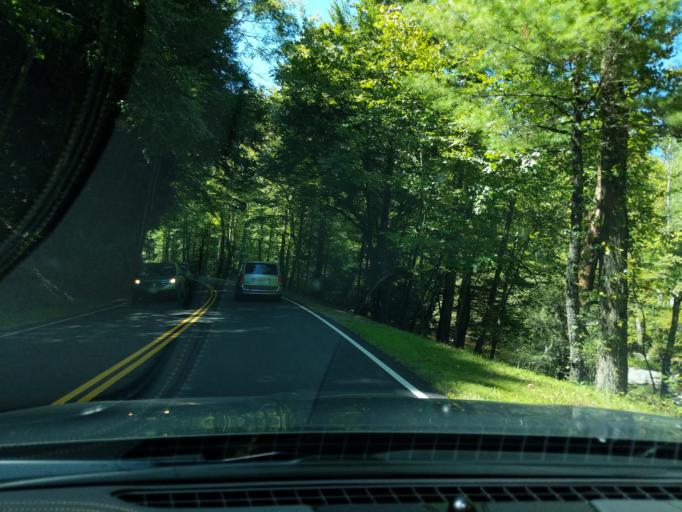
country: US
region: North Carolina
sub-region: Swain County
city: Cherokee
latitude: 35.5548
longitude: -83.3111
